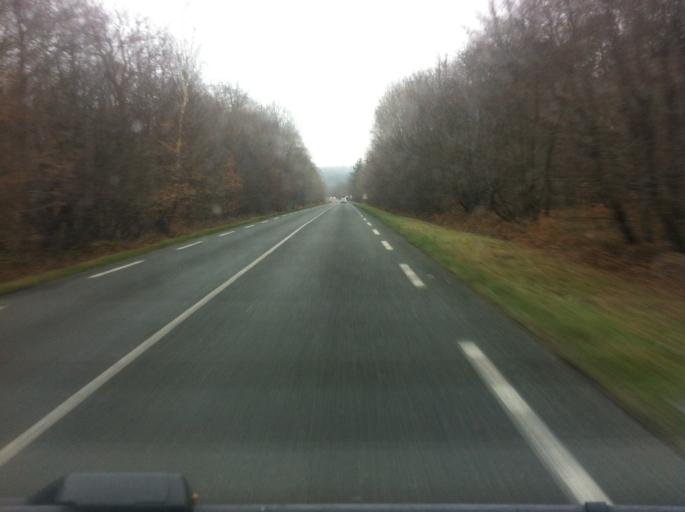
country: FR
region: Haute-Normandie
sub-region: Departement de la Seine-Maritime
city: Jumieges
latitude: 49.4448
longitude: 0.7880
